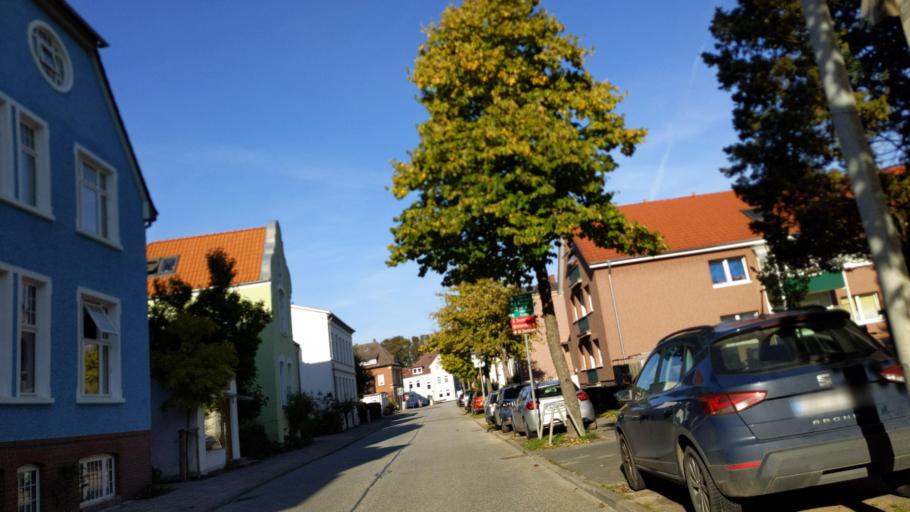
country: DE
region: Schleswig-Holstein
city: Eutin
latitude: 54.1308
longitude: 10.6127
